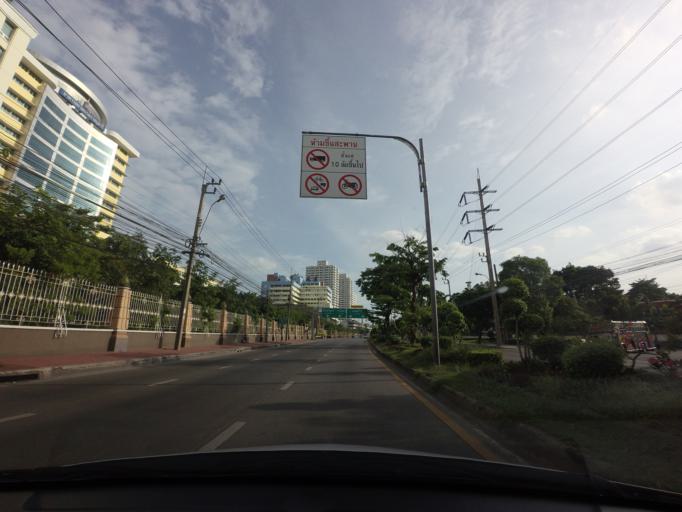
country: TH
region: Bangkok
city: Bang Kapi
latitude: 13.7711
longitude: 100.6534
